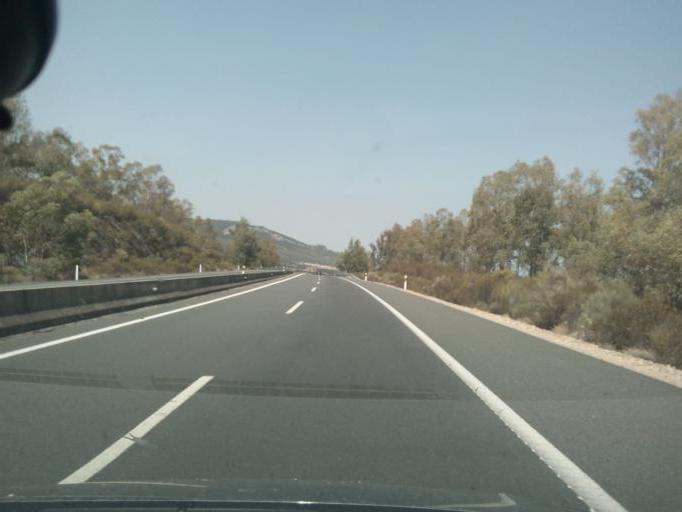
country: ES
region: Extremadura
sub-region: Provincia de Caceres
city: Romangordo
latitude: 39.7144
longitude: -5.7007
